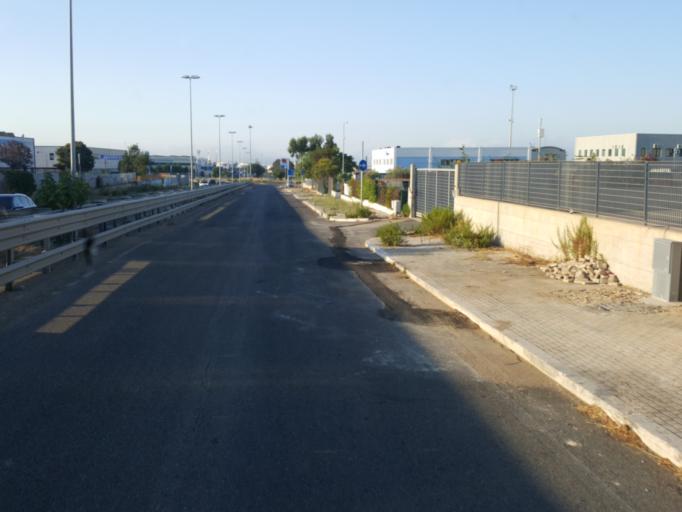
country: IT
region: Latium
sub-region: Citta metropolitana di Roma Capitale
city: Aurelia
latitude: 42.1226
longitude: 11.7781
